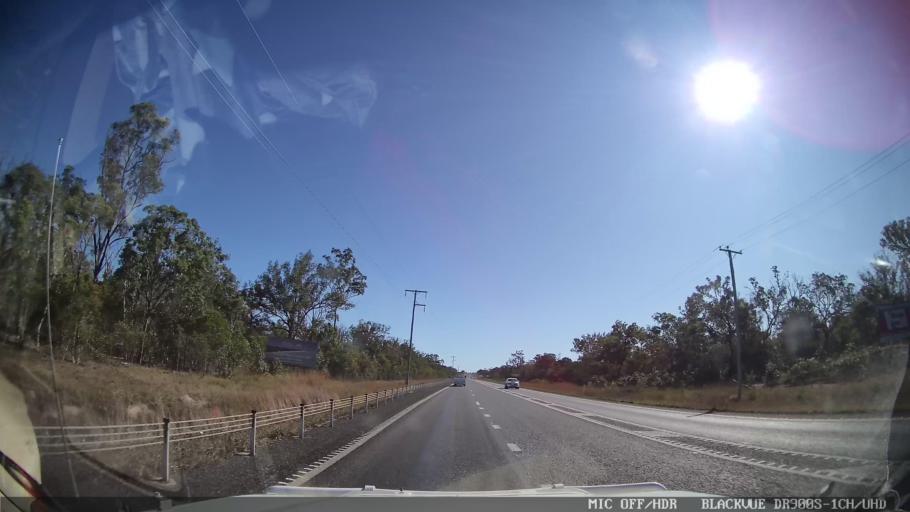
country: AU
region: Queensland
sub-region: Bundaberg
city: Childers
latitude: -25.2494
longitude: 152.3415
